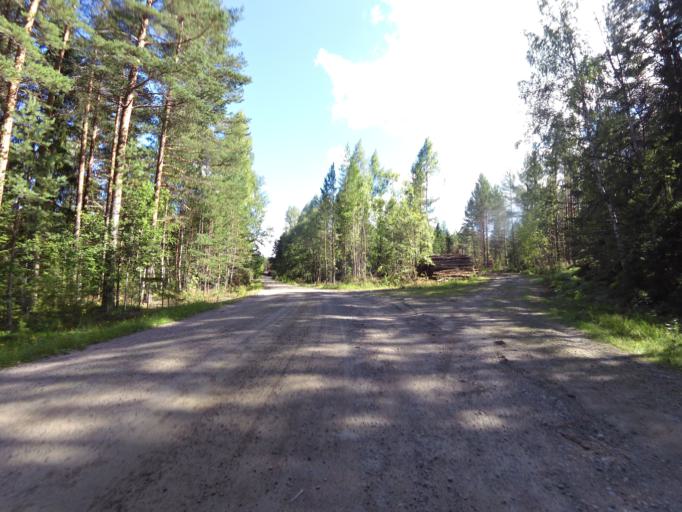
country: SE
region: Gaevleborg
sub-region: Hofors Kommun
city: Hofors
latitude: 60.5048
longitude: 16.3626
